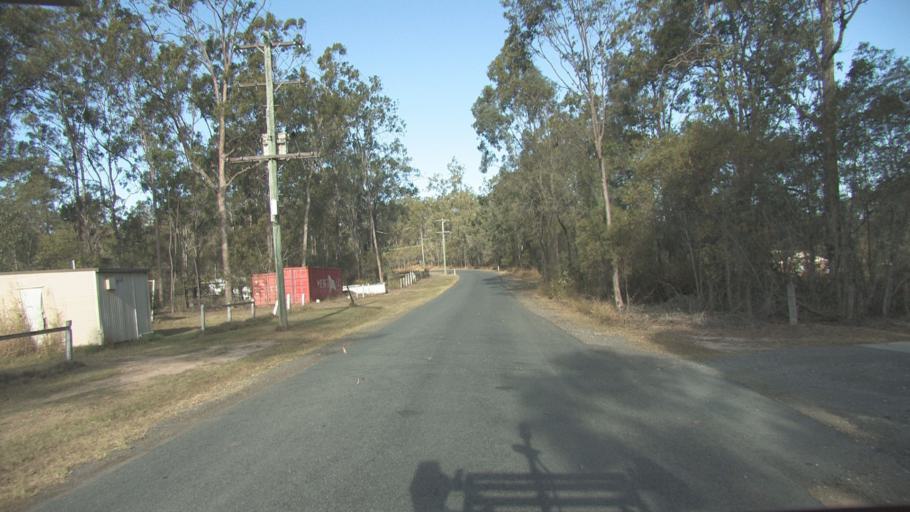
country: AU
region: Queensland
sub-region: Logan
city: Cedar Vale
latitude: -27.8443
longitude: 153.0576
